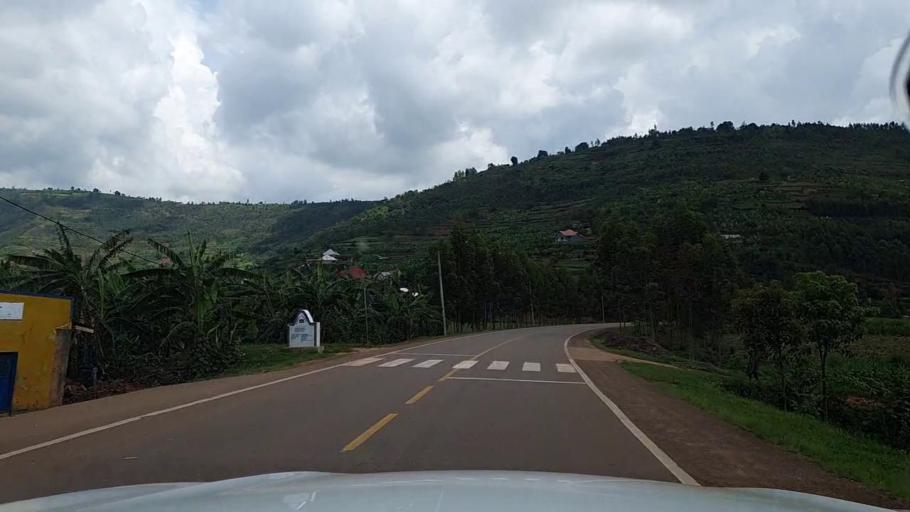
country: RW
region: Kigali
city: Kigali
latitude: -1.8129
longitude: 30.0970
